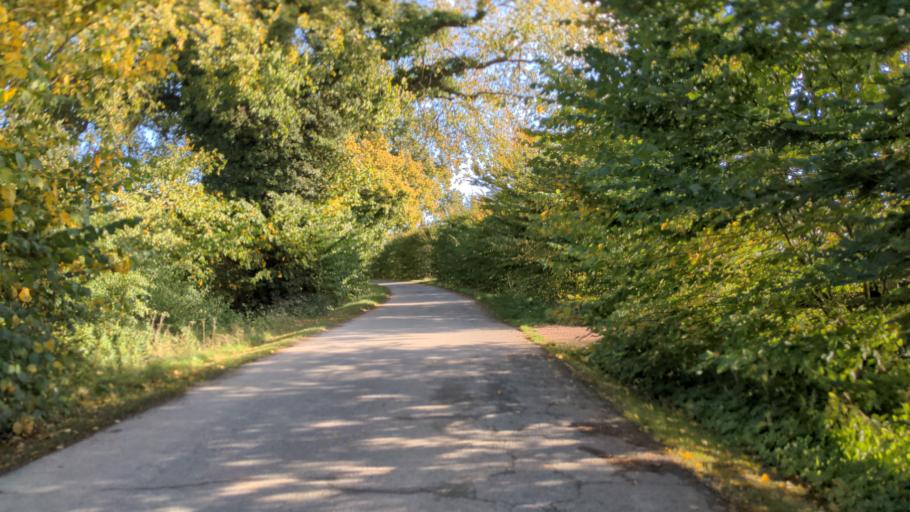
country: DE
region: Schleswig-Holstein
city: Manhagen
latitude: 54.1838
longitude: 10.9134
